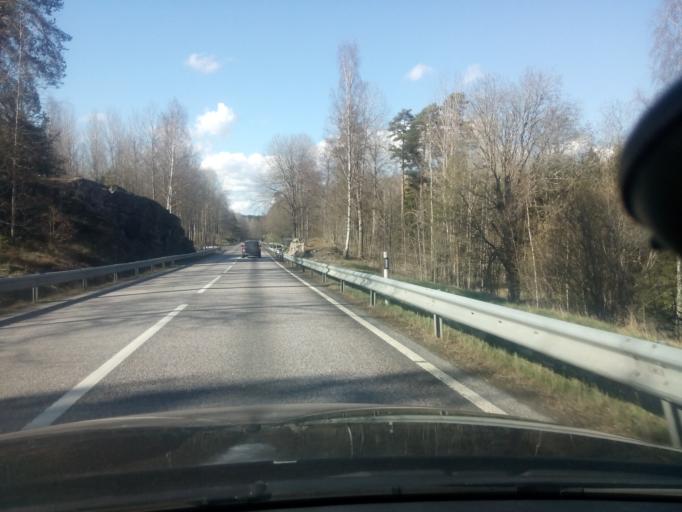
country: SE
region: Soedermanland
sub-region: Strangnas Kommun
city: Akers Styckebruk
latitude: 59.2513
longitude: 16.9410
